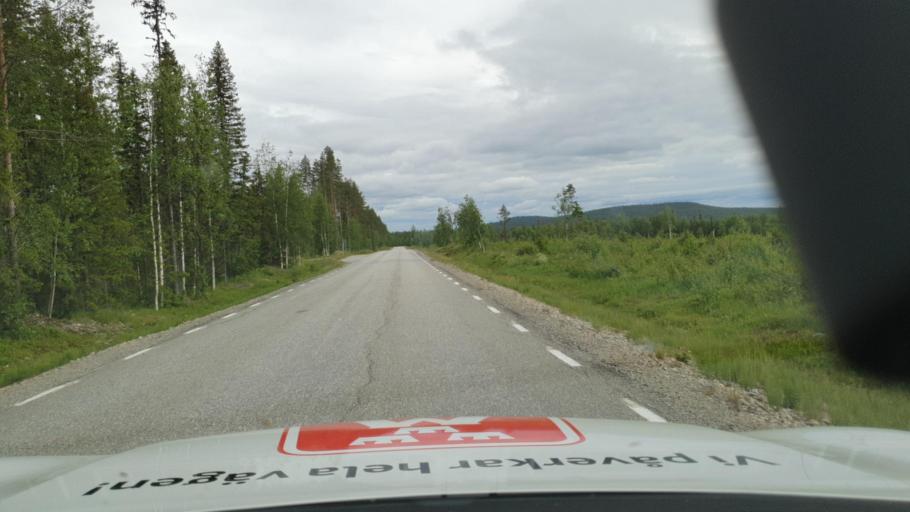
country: SE
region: Vaesterbotten
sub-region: Lycksele Kommun
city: Soderfors
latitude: 64.3429
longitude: 18.1376
